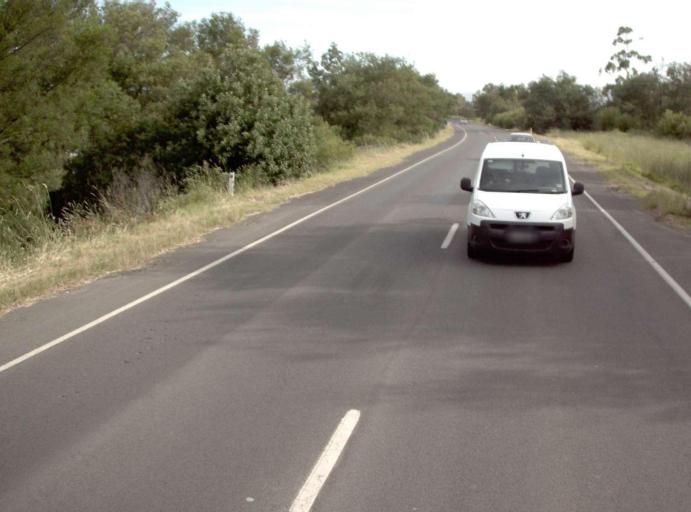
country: AU
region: Victoria
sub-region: Latrobe
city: Traralgon
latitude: -38.1537
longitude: 146.5539
